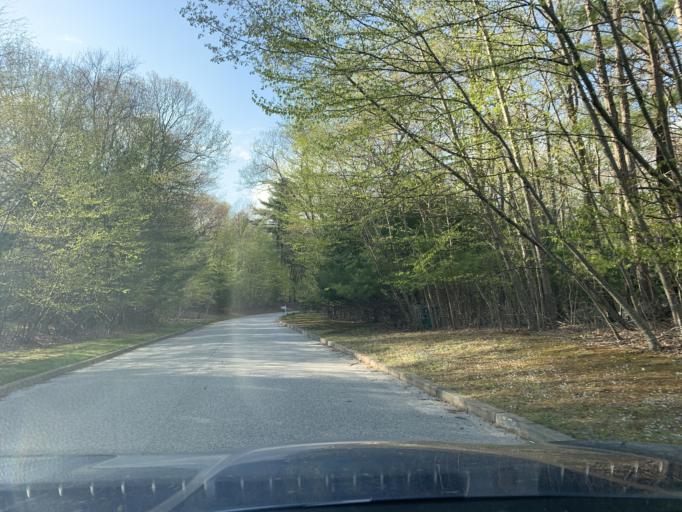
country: US
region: Rhode Island
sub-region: Washington County
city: Exeter
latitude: 41.6091
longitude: -71.5320
